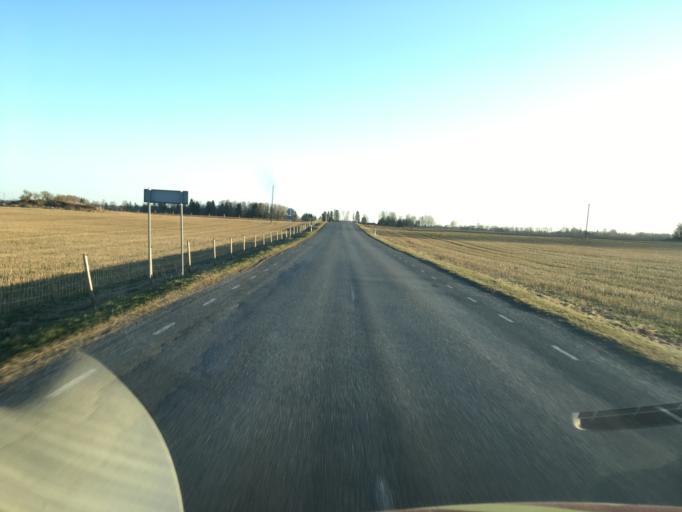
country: EE
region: Raplamaa
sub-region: Kehtna vald
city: Kehtna
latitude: 59.0198
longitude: 24.9252
